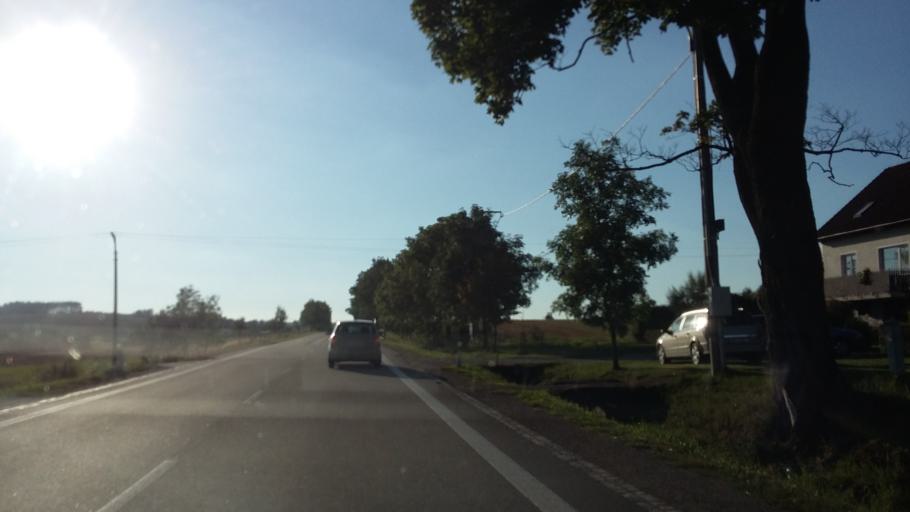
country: CZ
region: Vysocina
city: Merin
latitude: 49.3960
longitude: 15.8759
